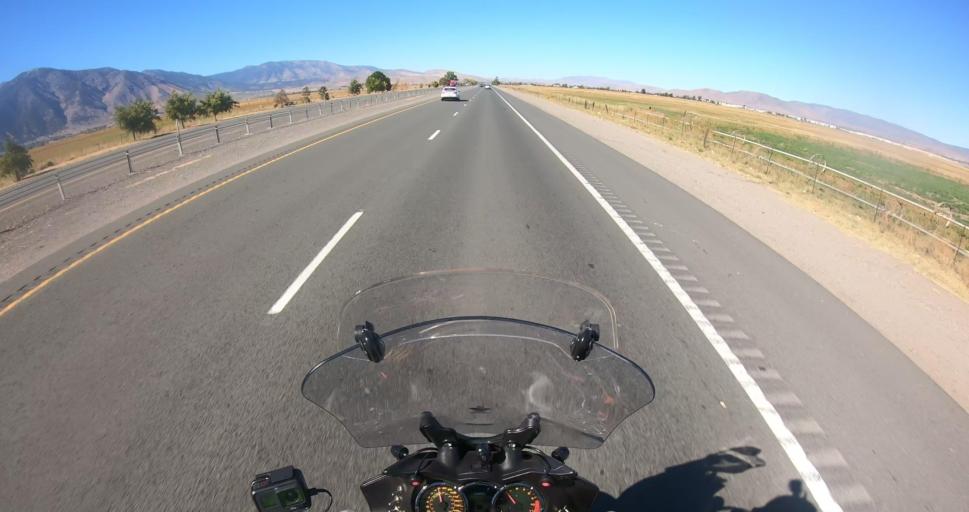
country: US
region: Nevada
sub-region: Douglas County
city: Minden
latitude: 38.9809
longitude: -119.7780
